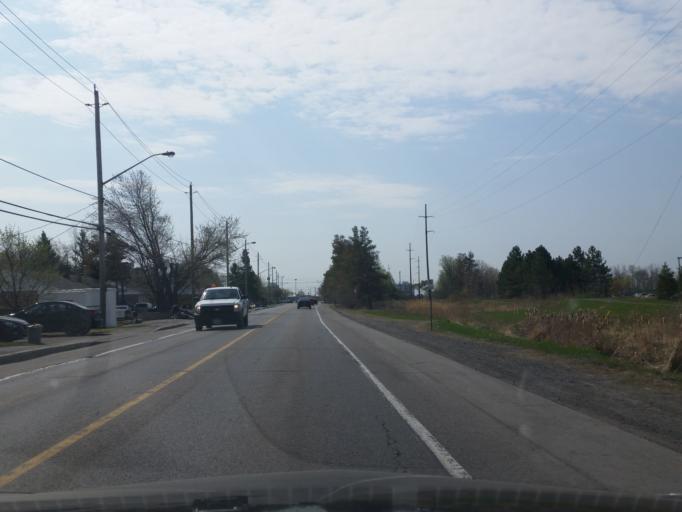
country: CA
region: Ontario
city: Ottawa
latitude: 45.4390
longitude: -75.6111
